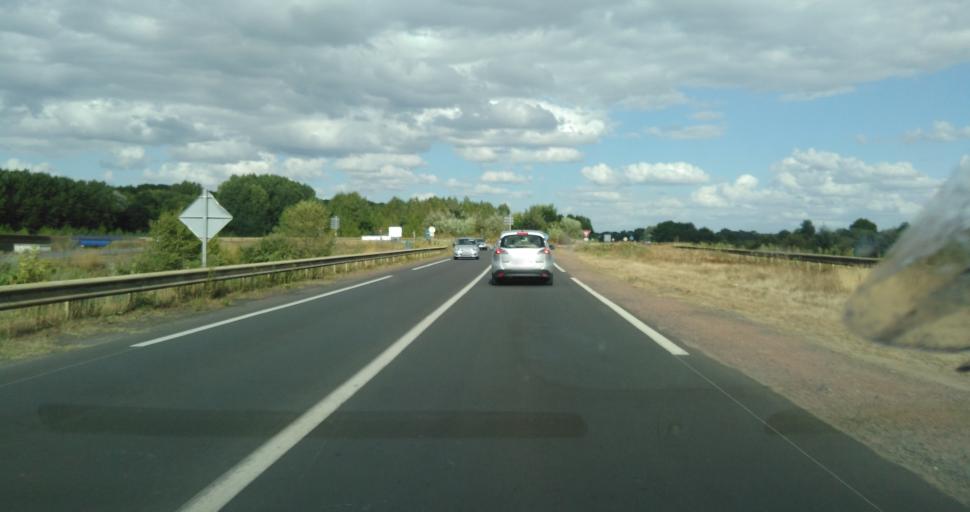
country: FR
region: Centre
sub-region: Departement d'Indre-et-Loire
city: Langeais
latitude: 47.3255
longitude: 0.4212
